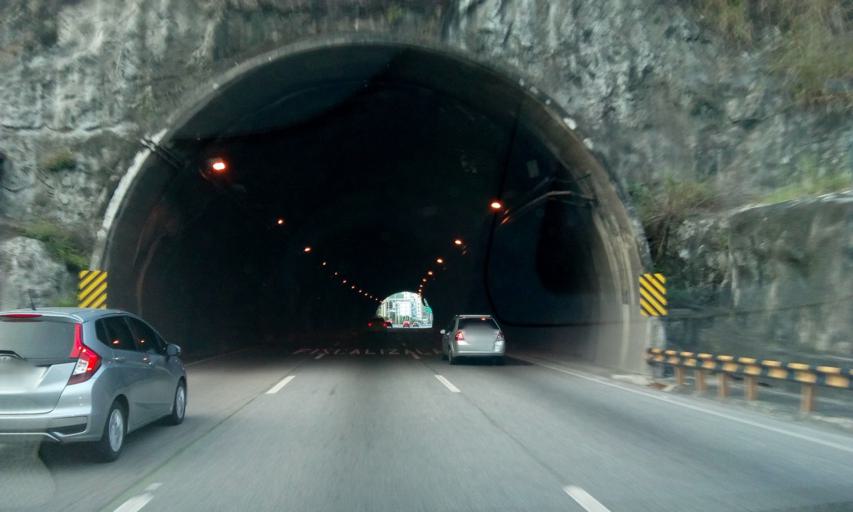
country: BR
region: Rio de Janeiro
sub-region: Sao Joao De Meriti
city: Sao Joao de Meriti
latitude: -22.9331
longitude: -43.3455
